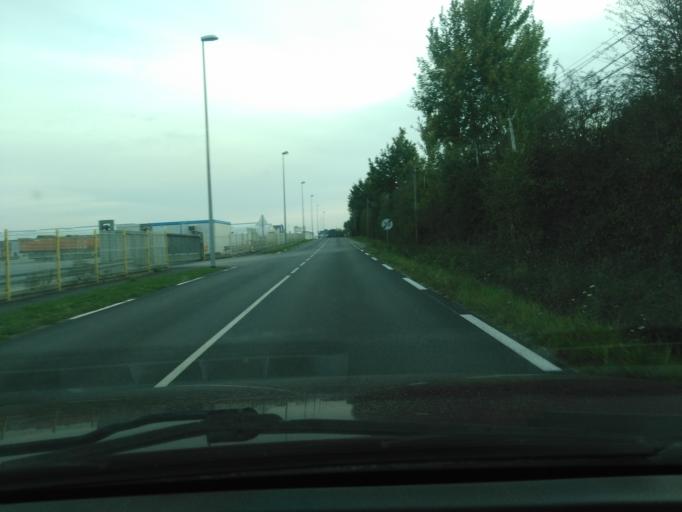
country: FR
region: Pays de la Loire
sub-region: Departement de la Vendee
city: Mouilleron-le-Captif
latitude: 46.7172
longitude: -1.4317
